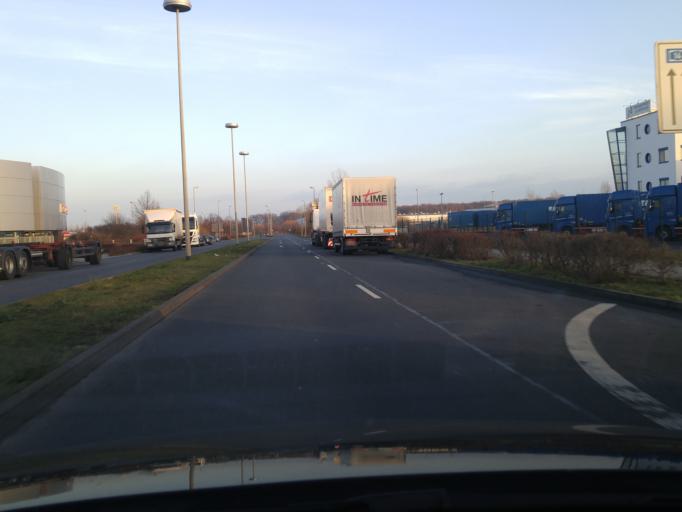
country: DE
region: Saxony
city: Zwochau
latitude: 51.4131
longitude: 12.3030
